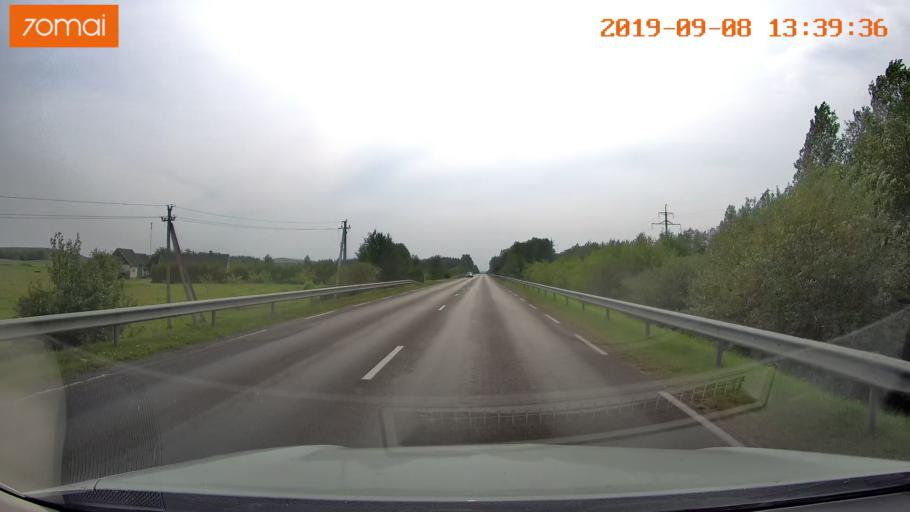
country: LT
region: Alytaus apskritis
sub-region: Alytus
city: Alytus
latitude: 54.4285
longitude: 24.1173
